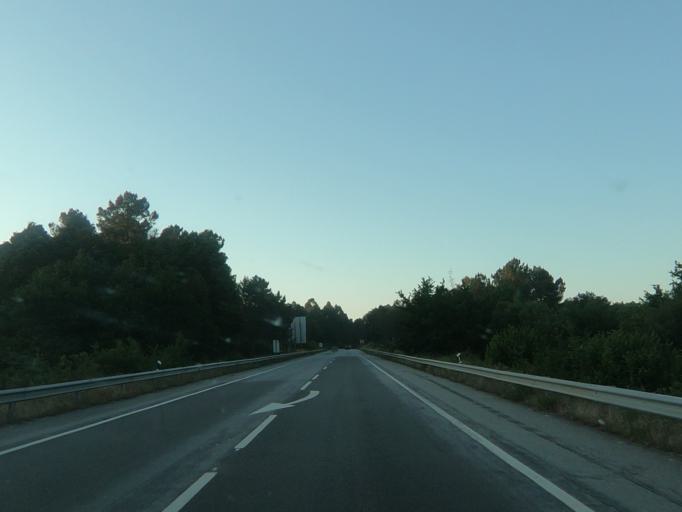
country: PT
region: Viseu
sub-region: Viseu
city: Rio de Loba
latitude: 40.6619
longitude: -7.8625
